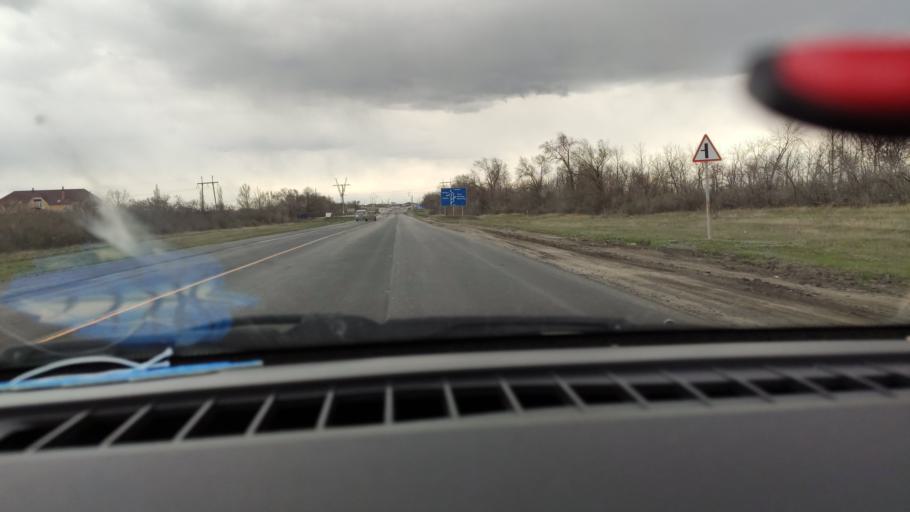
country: RU
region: Saratov
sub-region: Saratovskiy Rayon
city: Saratov
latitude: 51.6738
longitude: 46.0006
